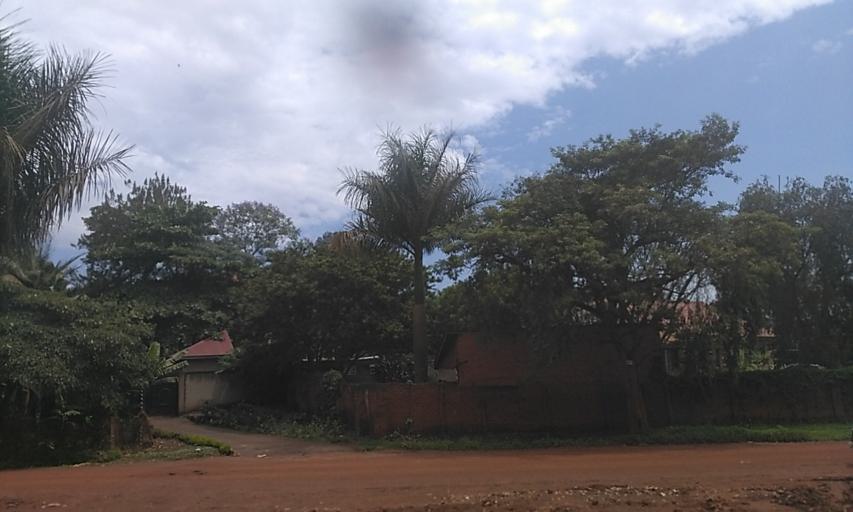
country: UG
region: Central Region
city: Kampala Central Division
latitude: 0.3118
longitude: 32.5164
